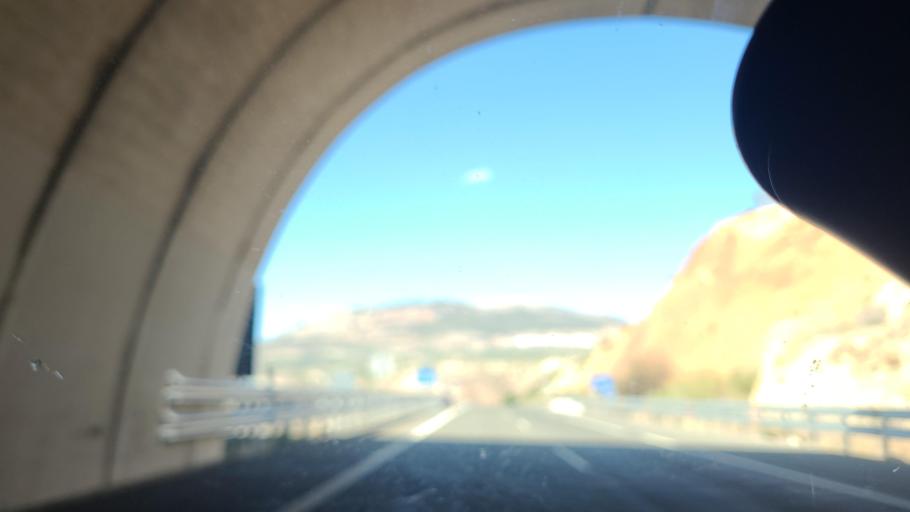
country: ES
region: Andalusia
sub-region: Provincia de Jaen
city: Pegalajar
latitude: 37.7034
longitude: -3.6362
